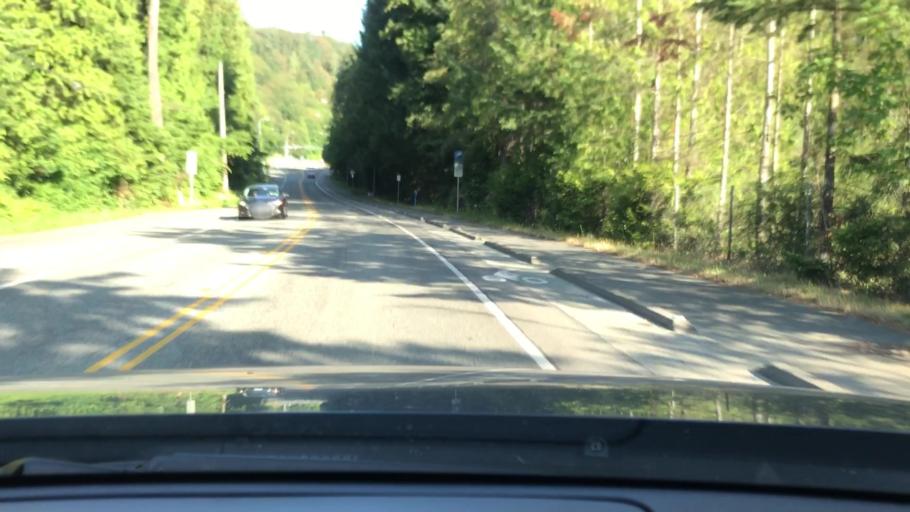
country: US
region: Washington
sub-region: King County
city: West Lake Sammamish
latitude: 47.5614
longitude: -122.0938
